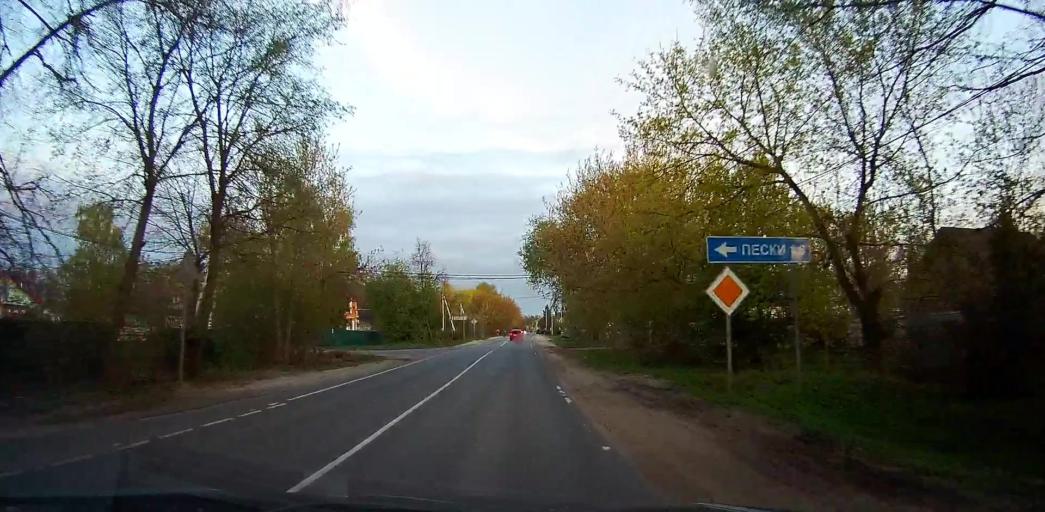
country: RU
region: Moskovskaya
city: Peski
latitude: 55.2069
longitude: 38.7395
